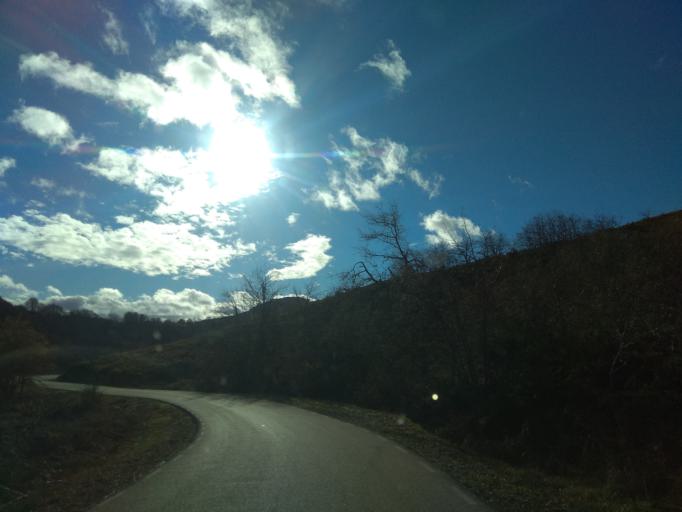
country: ES
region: Cantabria
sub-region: Provincia de Cantabria
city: San Martin de Elines
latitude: 42.9335
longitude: -3.8355
